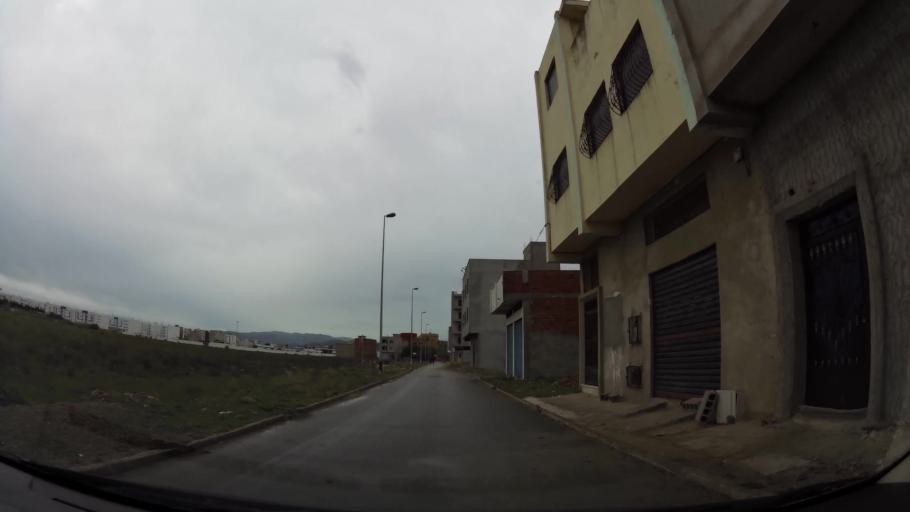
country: MA
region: Tanger-Tetouan
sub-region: Tetouan
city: Martil
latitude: 35.6166
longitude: -5.2982
